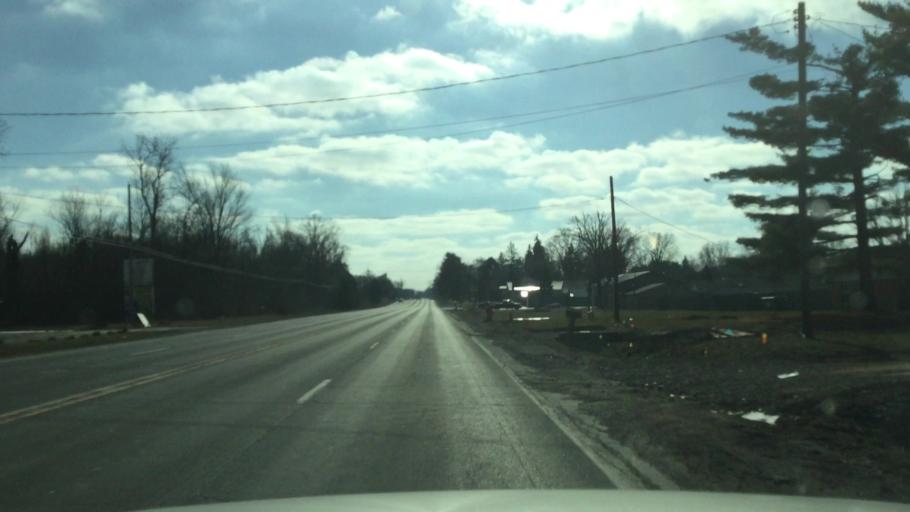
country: US
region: Michigan
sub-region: Genesee County
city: Mount Morris
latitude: 43.1152
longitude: -83.6761
